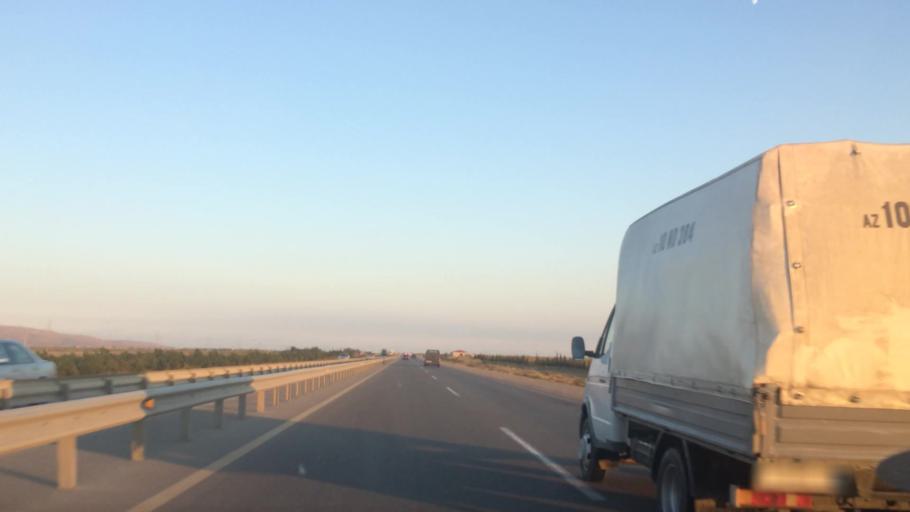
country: AZ
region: Baki
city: Qobustan
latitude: 39.9884
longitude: 49.2028
